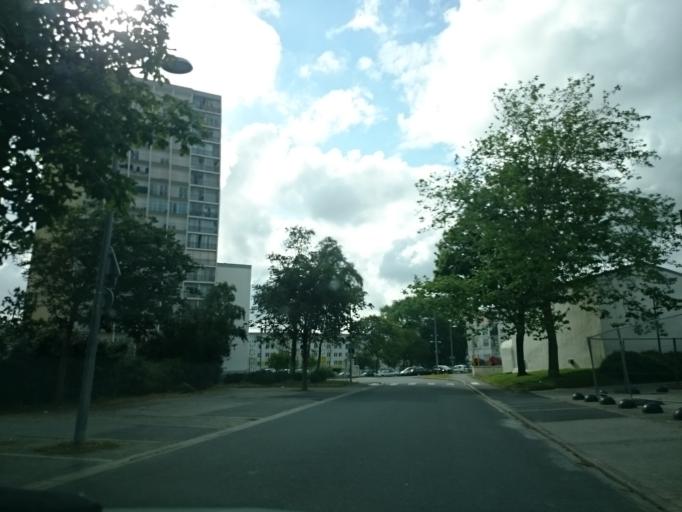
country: FR
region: Brittany
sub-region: Departement du Finistere
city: Brest
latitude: 48.4125
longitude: -4.4727
